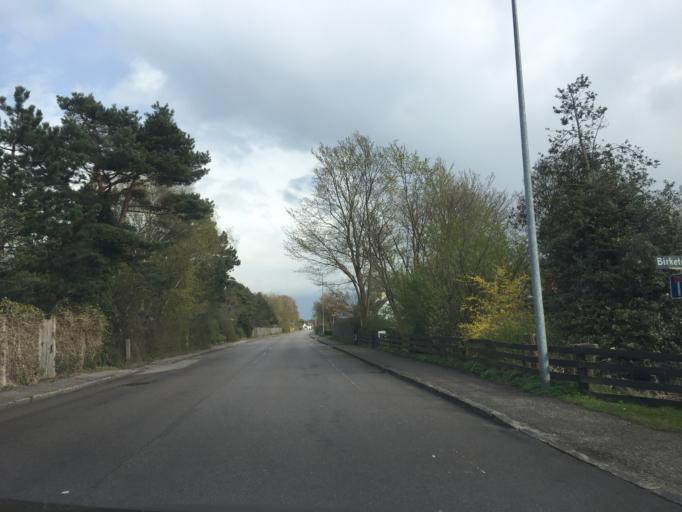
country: DK
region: Capital Region
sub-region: Halsnaes Kommune
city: Liseleje
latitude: 56.0108
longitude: 11.9780
